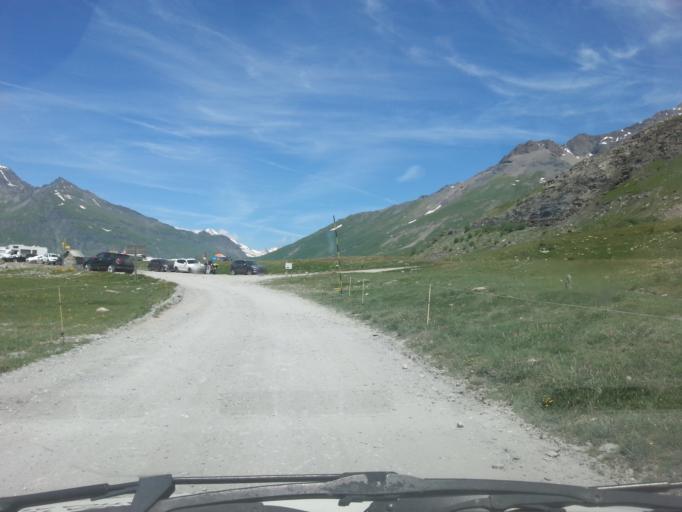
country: IT
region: Piedmont
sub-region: Provincia di Torino
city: Moncenisio
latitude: 45.2246
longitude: 6.9635
